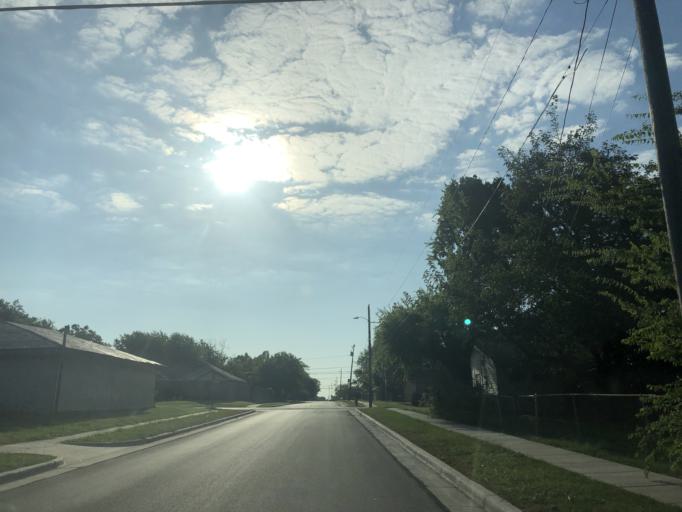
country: US
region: Texas
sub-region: Dallas County
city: Grand Prairie
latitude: 32.7331
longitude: -97.0391
